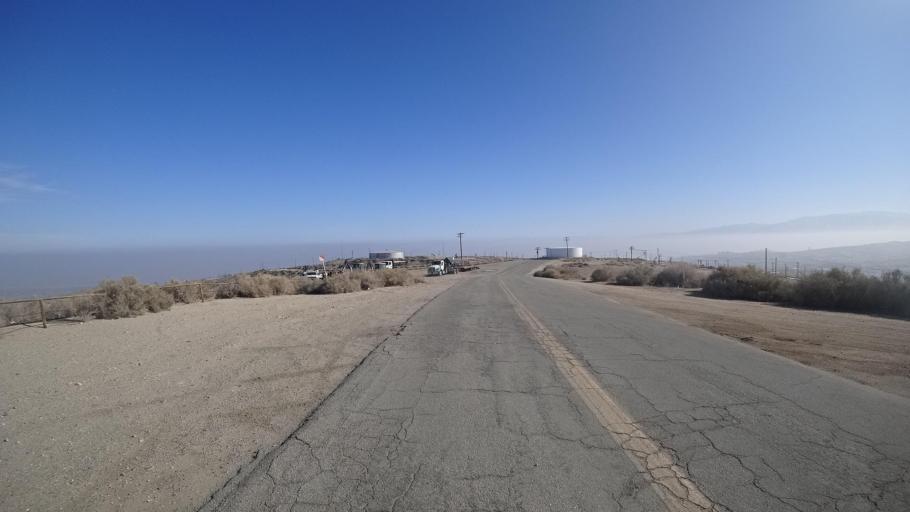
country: US
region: California
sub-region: Kern County
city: Taft Heights
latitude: 35.1147
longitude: -119.4684
